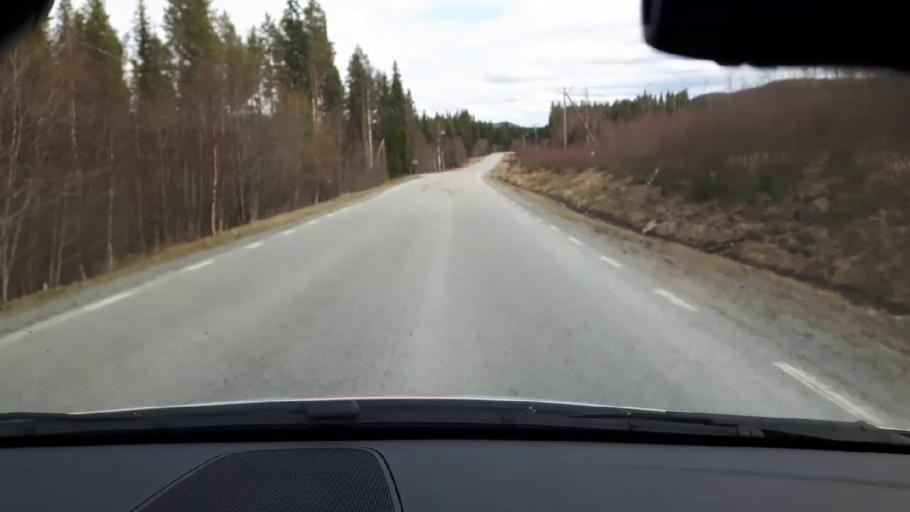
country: SE
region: Jaemtland
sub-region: Bergs Kommun
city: Hoverberg
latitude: 62.6649
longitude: 14.7312
